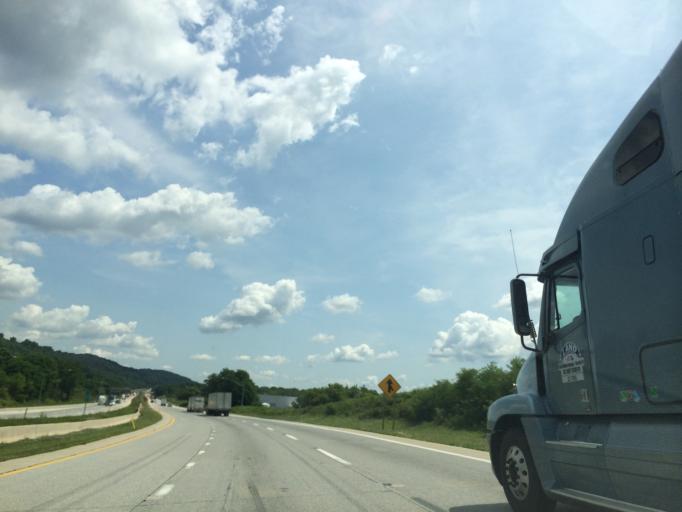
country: US
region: Pennsylvania
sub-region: Lehigh County
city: Fountain Hill
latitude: 40.5552
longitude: -75.4284
